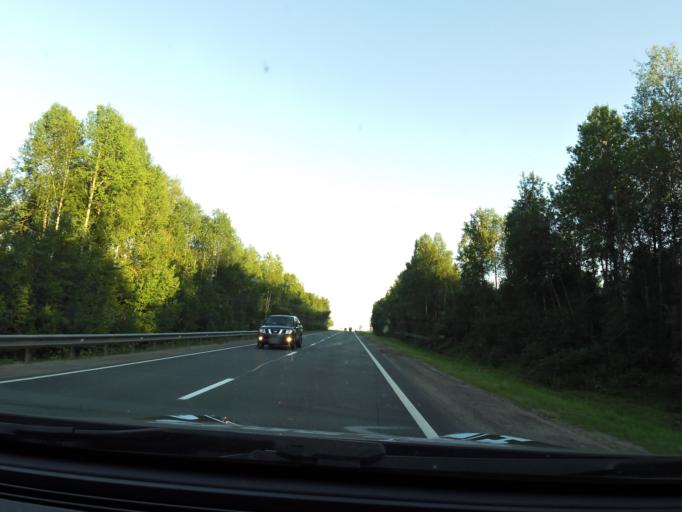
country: RU
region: Vologda
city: Gryazovets
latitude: 58.6642
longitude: 40.3137
